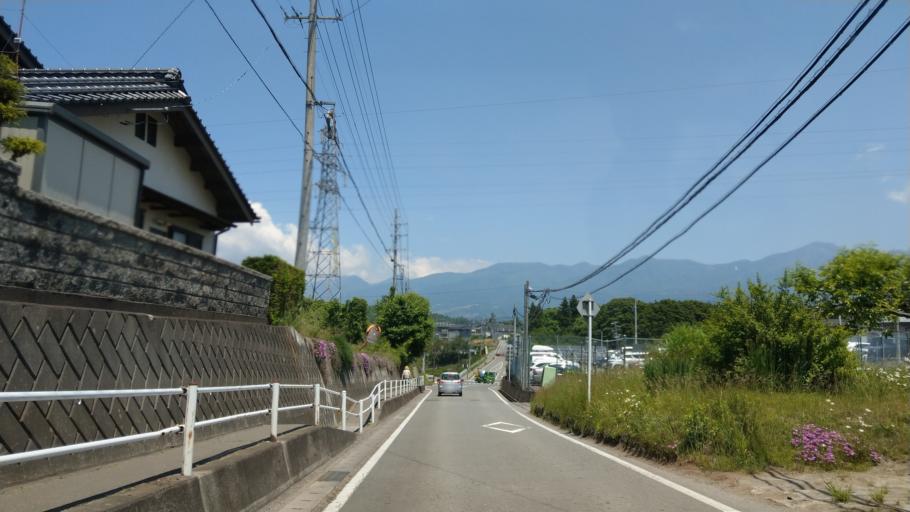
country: JP
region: Nagano
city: Komoro
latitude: 36.2921
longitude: 138.4400
